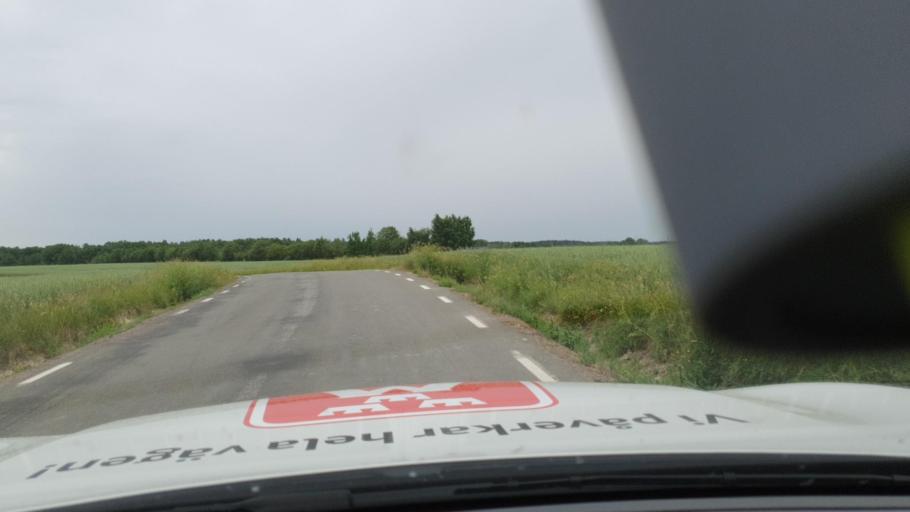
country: SE
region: Vaestra Goetaland
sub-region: Tidaholms Kommun
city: Olofstorp
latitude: 58.3044
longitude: 14.0639
